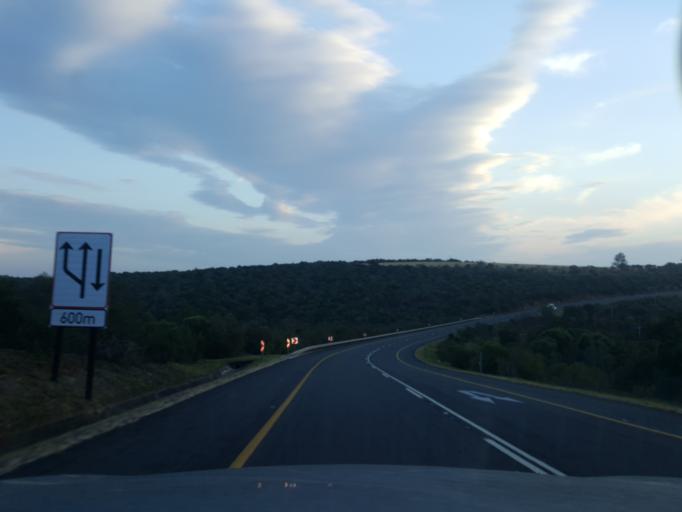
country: ZA
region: Eastern Cape
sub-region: Cacadu District Municipality
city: Grahamstown
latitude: -33.3786
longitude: 26.4652
